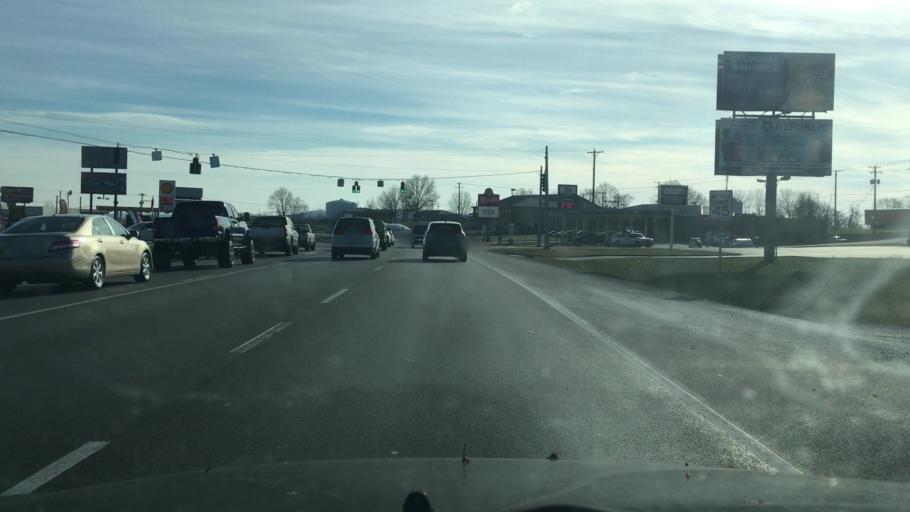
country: US
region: Kentucky
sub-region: Pulaski County
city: Somerset
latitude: 37.0179
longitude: -84.6279
